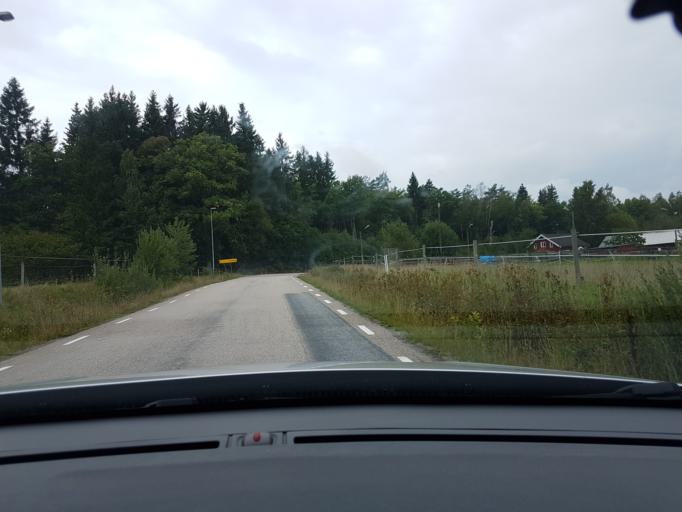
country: SE
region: Vaestra Goetaland
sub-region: Ale Kommun
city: Alvangen
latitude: 57.9183
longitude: 12.1346
